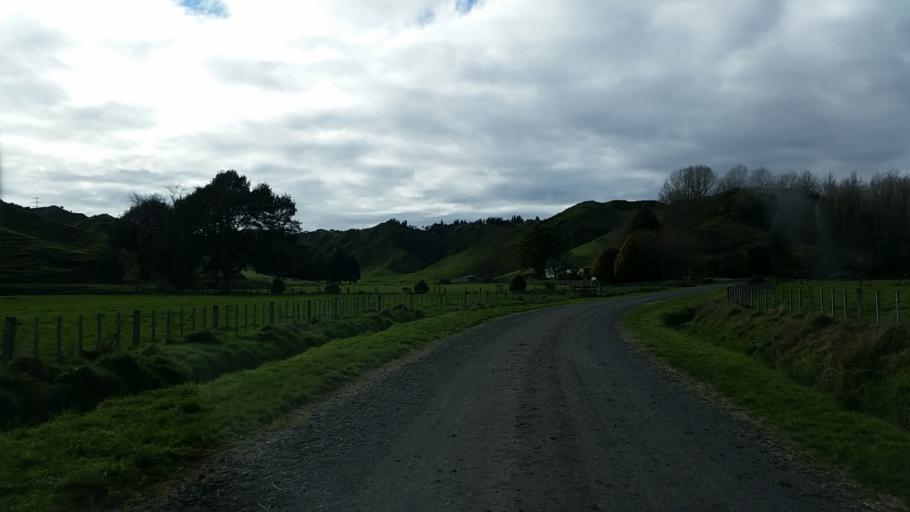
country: NZ
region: Taranaki
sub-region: South Taranaki District
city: Eltham
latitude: -39.2502
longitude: 174.5385
